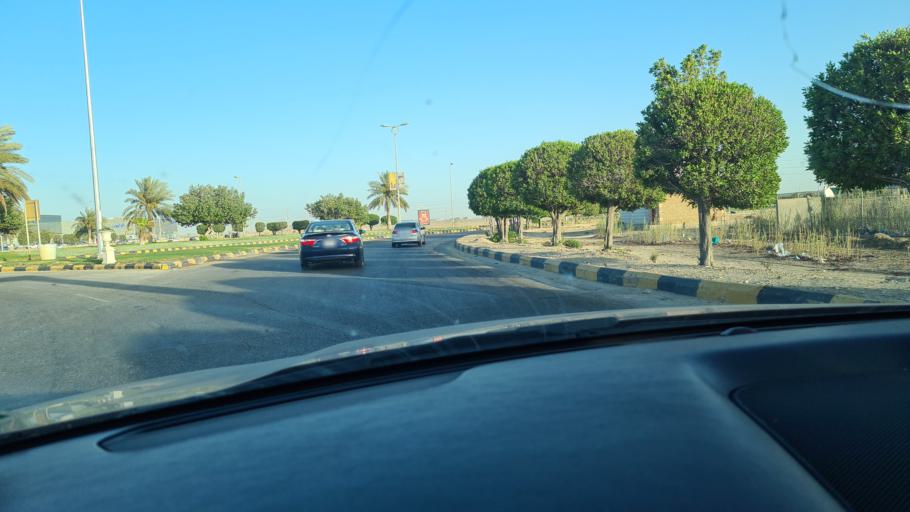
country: SA
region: Eastern Province
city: Al Jubayl
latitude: 26.9268
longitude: 49.7112
